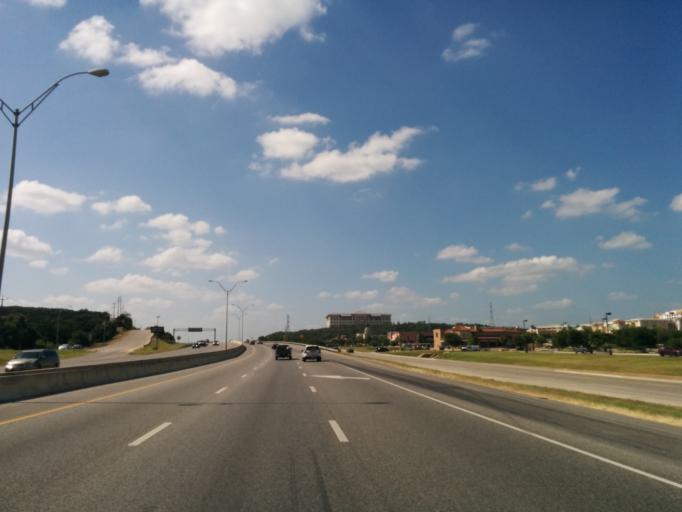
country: US
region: Texas
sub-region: Bexar County
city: Shavano Park
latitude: 29.6095
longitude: -98.6031
